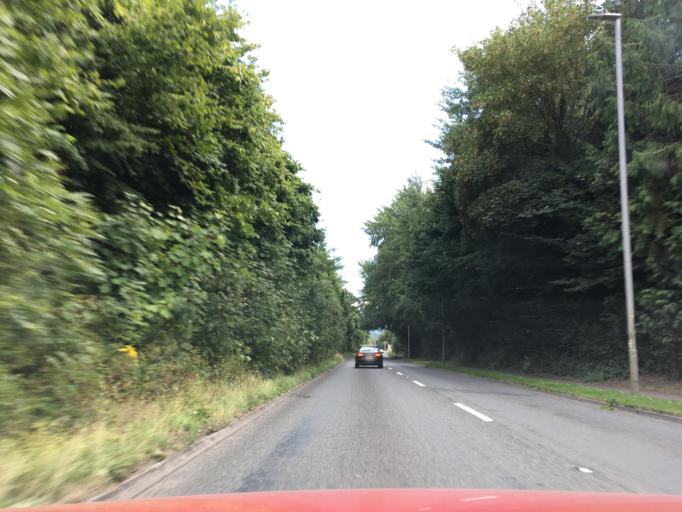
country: GB
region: England
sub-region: Somerset
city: Yeovil
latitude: 50.9261
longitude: -2.6373
